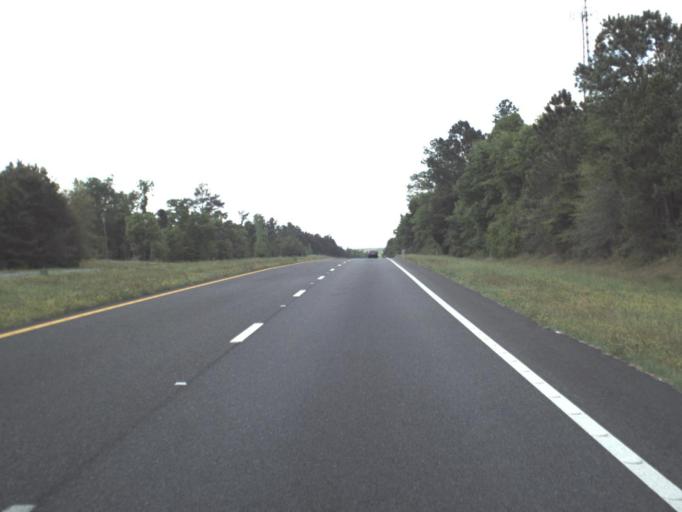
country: US
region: Florida
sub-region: Escambia County
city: Molino
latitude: 30.8550
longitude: -87.3229
